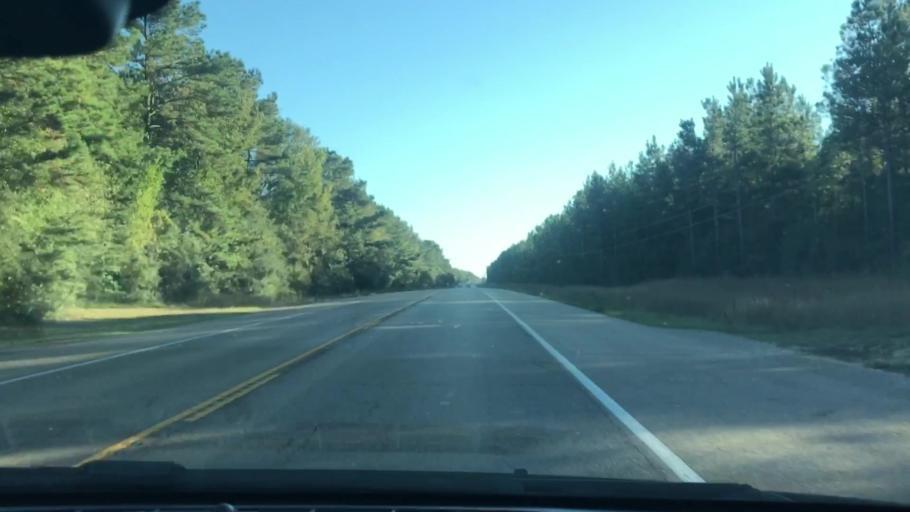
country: US
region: Louisiana
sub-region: Saint Tammany Parish
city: Abita Springs
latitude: 30.5847
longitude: -89.8715
